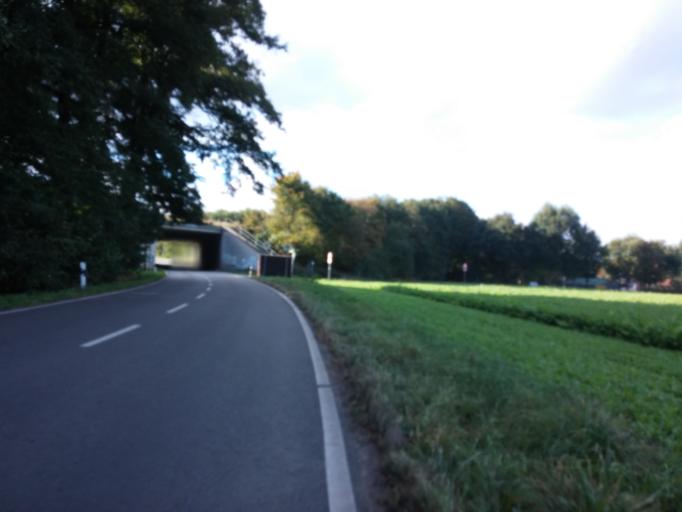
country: DE
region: North Rhine-Westphalia
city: Dorsten
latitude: 51.6264
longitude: 6.9355
